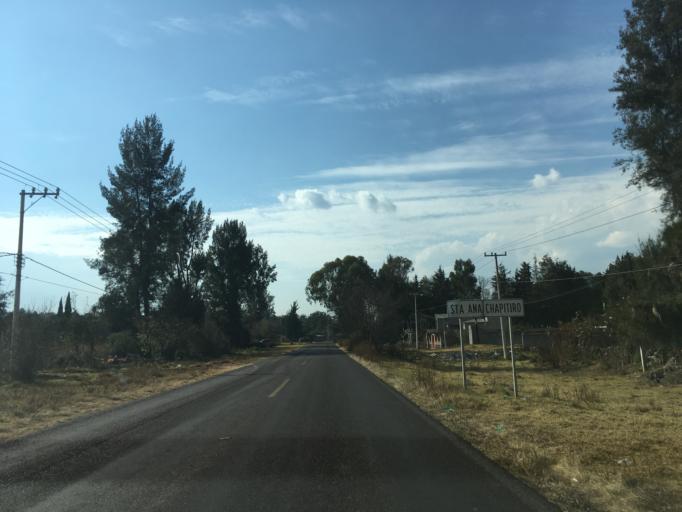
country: MX
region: Michoacan
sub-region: Patzcuaro
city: Santa Ana Chapitiro
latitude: 19.5283
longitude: -101.6490
